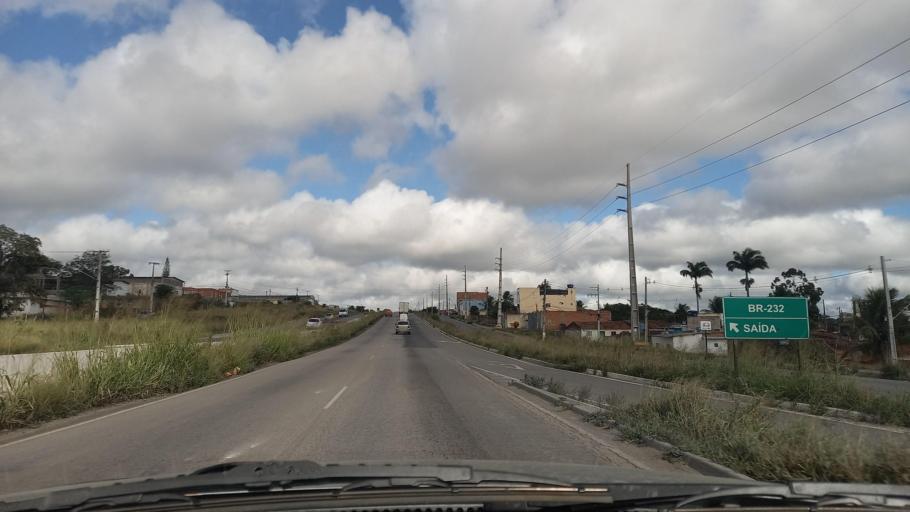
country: BR
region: Pernambuco
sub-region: Caruaru
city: Caruaru
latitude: -8.3065
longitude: -36.0171
